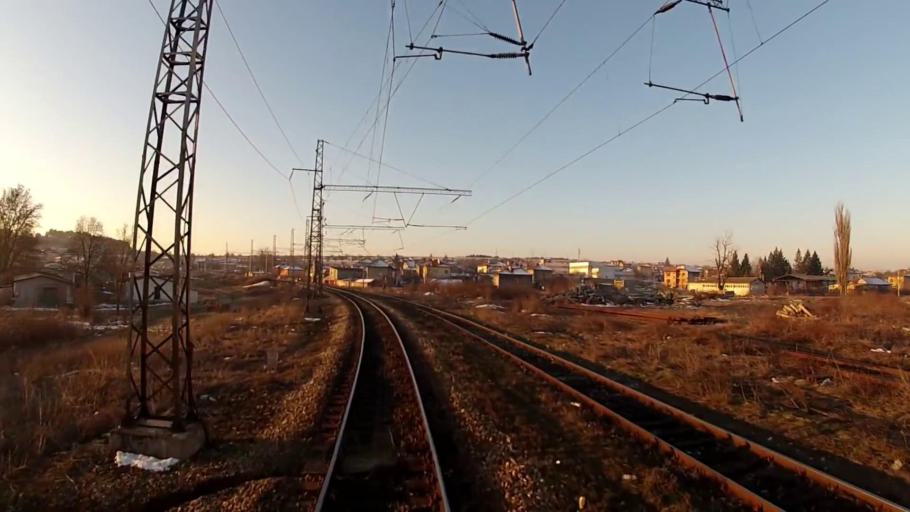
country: BG
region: Sofiya
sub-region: Obshtina Dragoman
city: Dragoman
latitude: 42.9160
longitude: 22.9335
